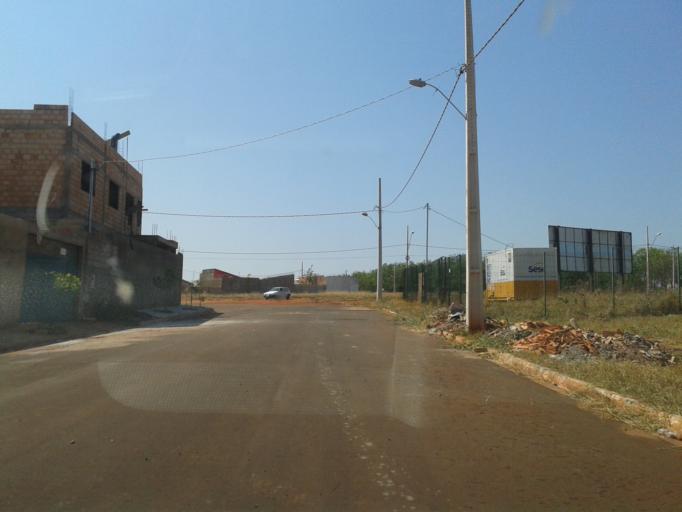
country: BR
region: Minas Gerais
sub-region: Ituiutaba
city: Ituiutaba
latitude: -19.0168
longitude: -49.4595
